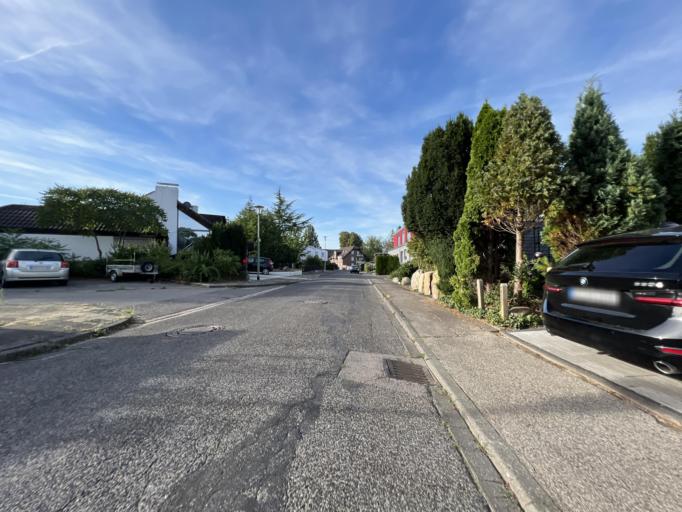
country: DE
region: North Rhine-Westphalia
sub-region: Regierungsbezirk Koln
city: Kreuzau
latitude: 50.7613
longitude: 6.4798
